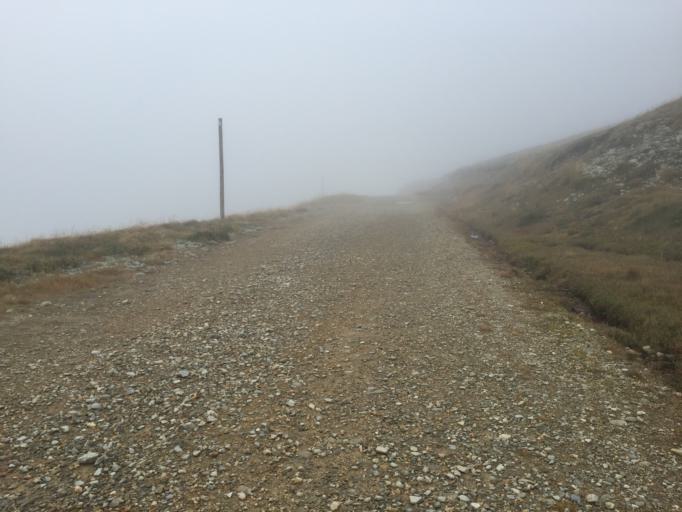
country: AU
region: New South Wales
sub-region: Snowy River
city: Jindabyne
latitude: -36.4524
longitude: 148.2747
